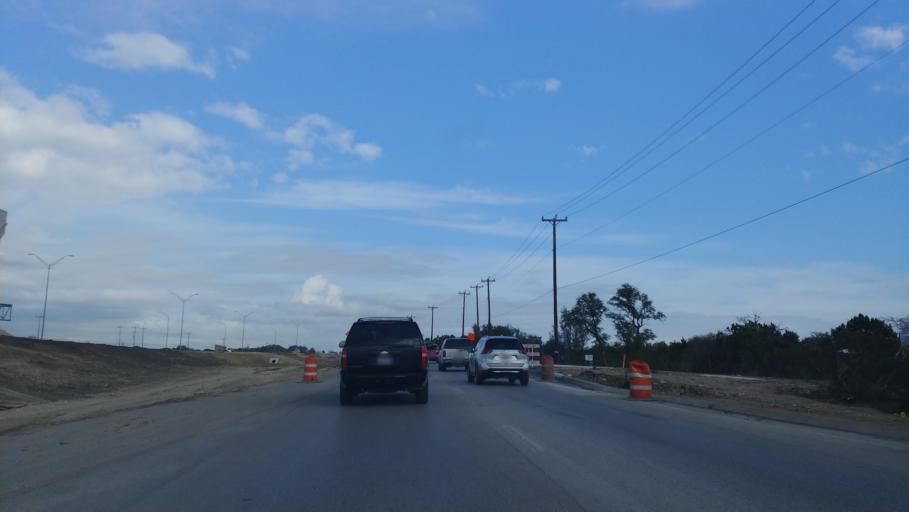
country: US
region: Texas
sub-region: Bexar County
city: Leon Valley
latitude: 29.4492
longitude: -98.7109
